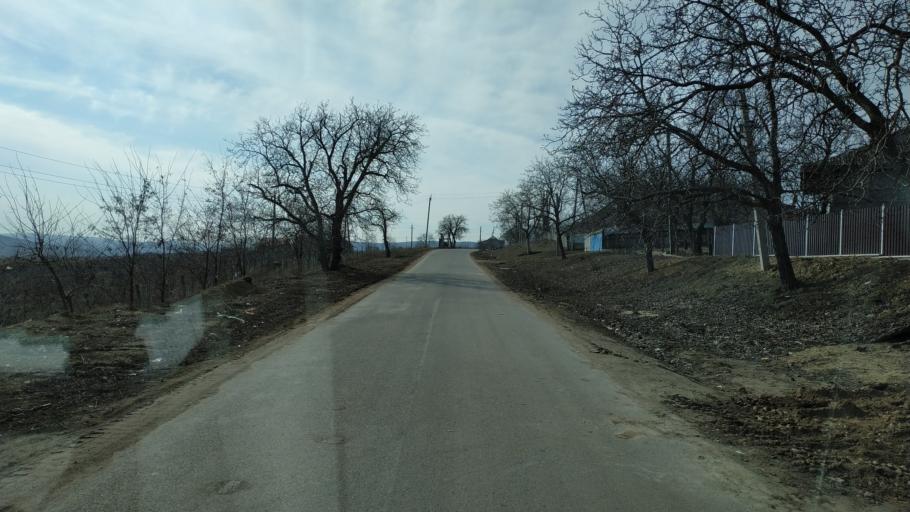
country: MD
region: Nisporeni
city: Nisporeni
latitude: 47.1514
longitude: 28.1287
